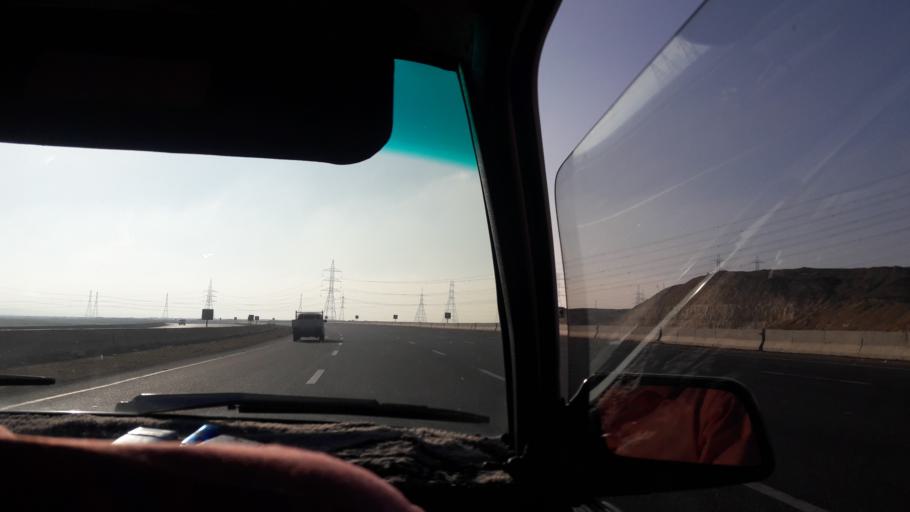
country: EG
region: Muhafazat al Qahirah
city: Halwan
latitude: 29.9042
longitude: 31.4954
